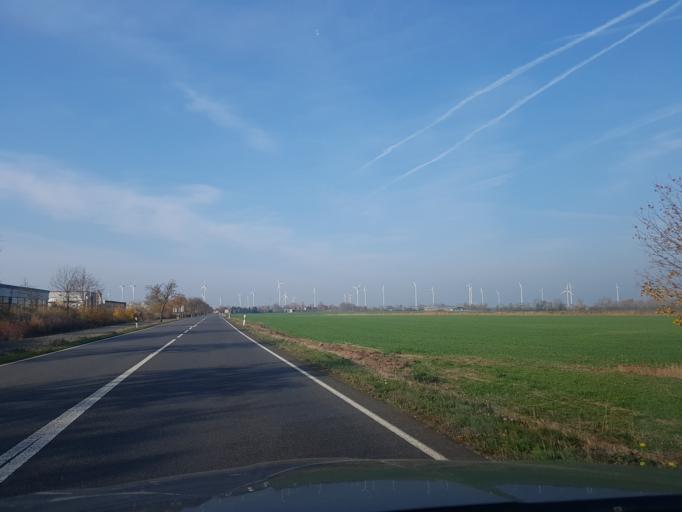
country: DE
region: Brandenburg
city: Bad Liebenwerda
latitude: 51.5105
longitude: 13.3628
